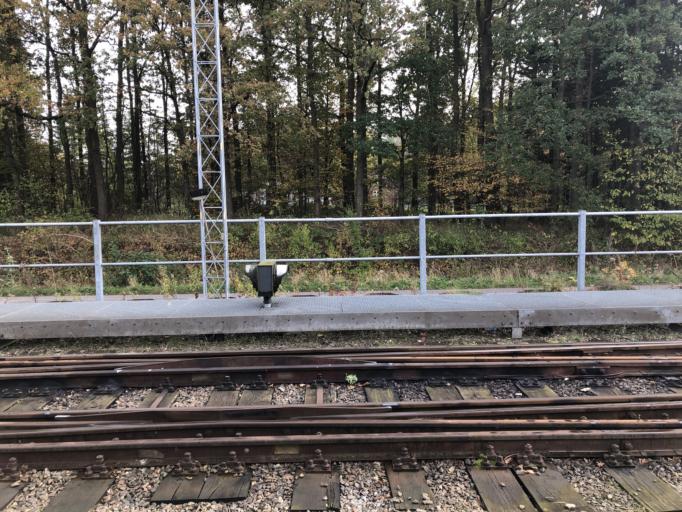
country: DK
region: Zealand
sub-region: Guldborgsund Kommune
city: Nykobing Falster
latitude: 54.7750
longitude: 11.8842
